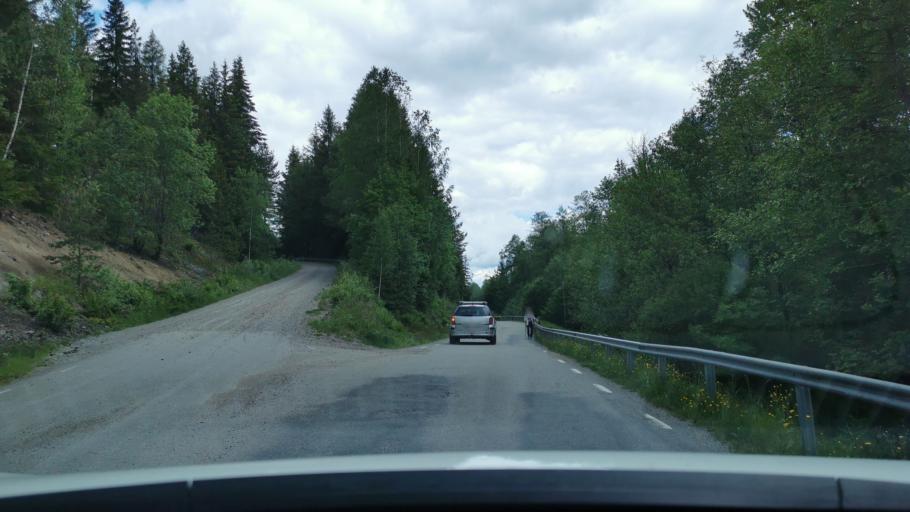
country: SE
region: Vaestra Goetaland
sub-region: Bengtsfors Kommun
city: Dals Langed
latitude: 58.8230
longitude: 12.3286
